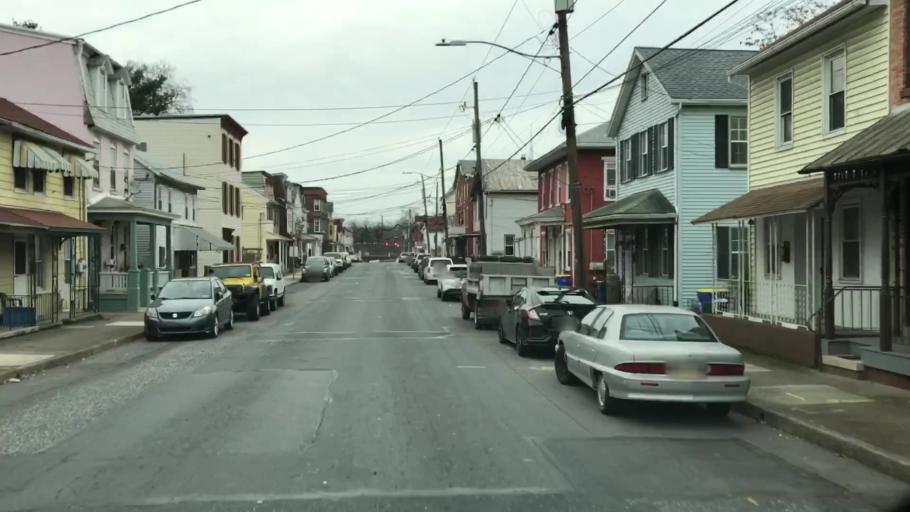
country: US
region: Pennsylvania
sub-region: Dauphin County
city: Middletown
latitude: 40.1935
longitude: -76.7351
